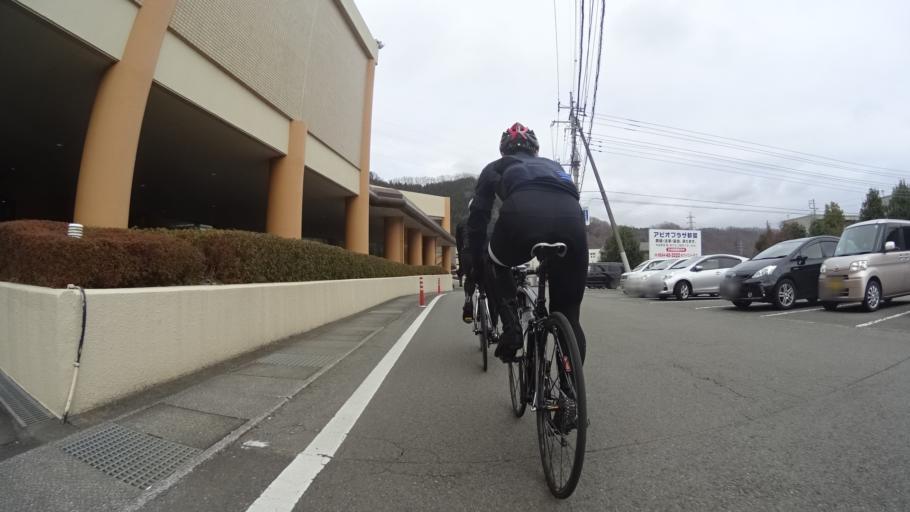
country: JP
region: Yamanashi
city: Otsuki
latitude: 35.5930
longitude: 138.9282
